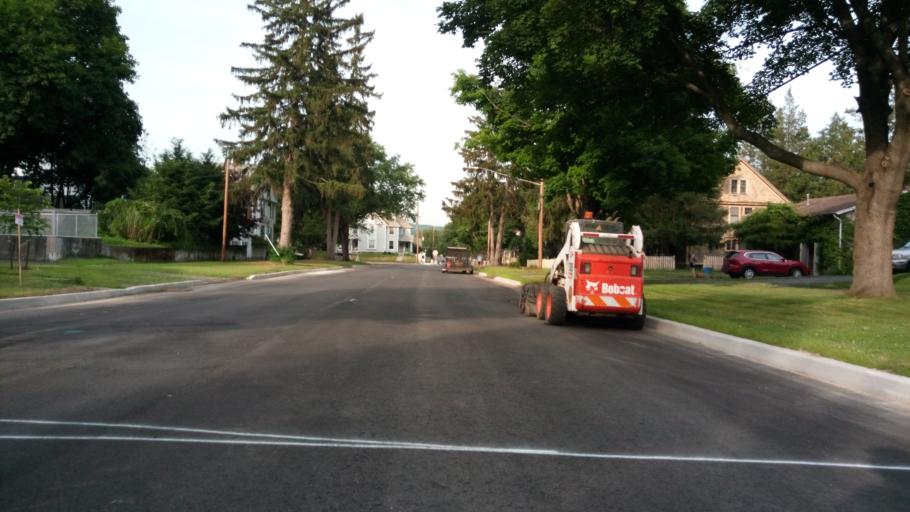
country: US
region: New York
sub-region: Chemung County
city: Elmira
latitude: 42.0874
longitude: -76.8235
